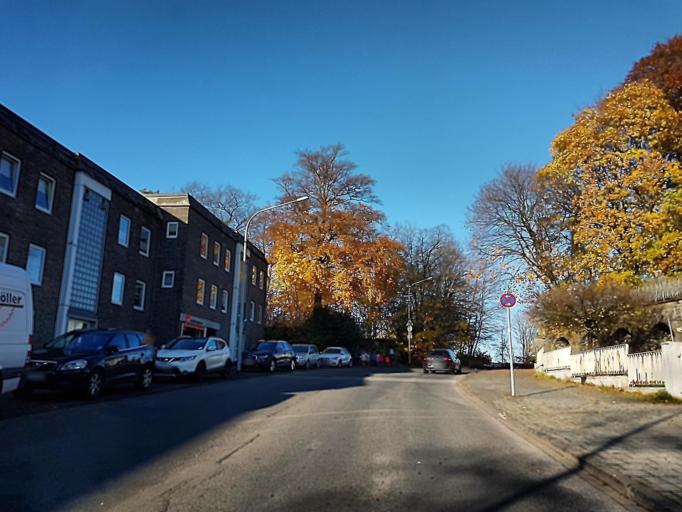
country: DE
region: North Rhine-Westphalia
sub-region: Regierungsbezirk Dusseldorf
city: Remscheid
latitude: 51.1947
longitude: 7.2525
